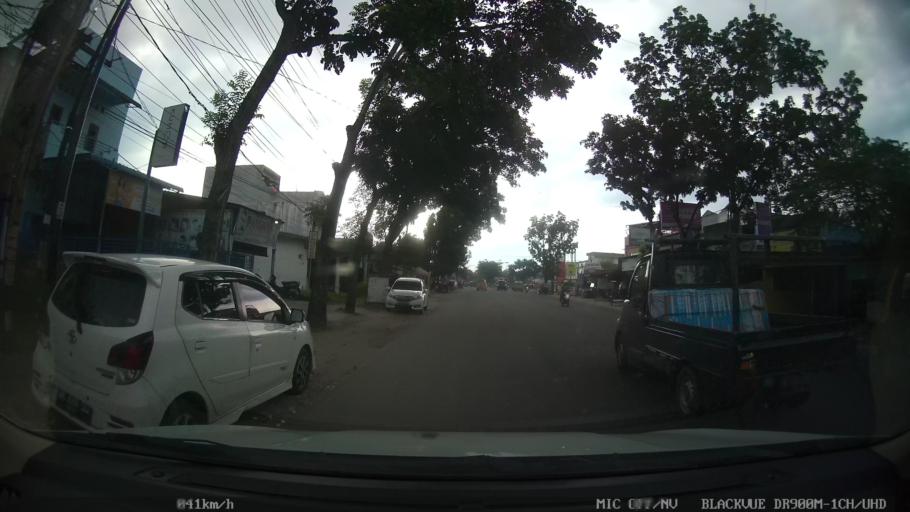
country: ID
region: North Sumatra
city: Sunggal
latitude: 3.5402
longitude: 98.6257
